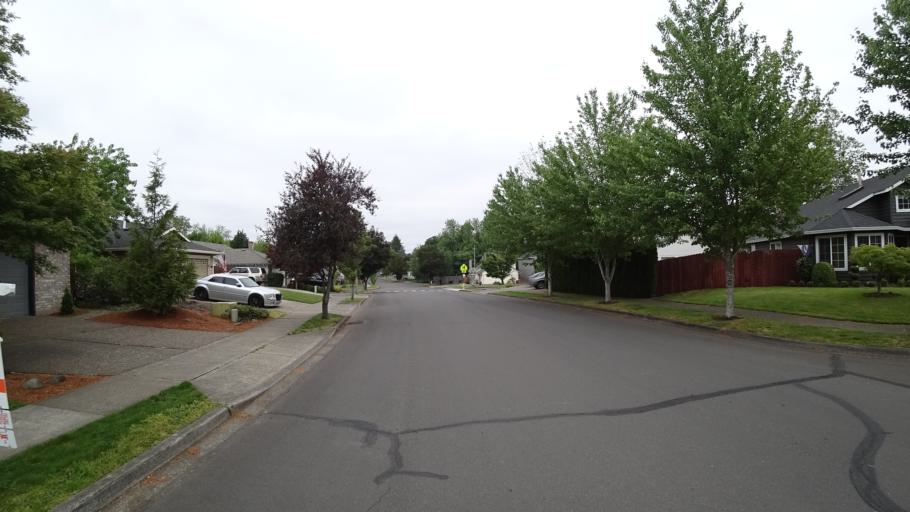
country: US
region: Oregon
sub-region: Washington County
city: Aloha
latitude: 45.5058
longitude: -122.9068
